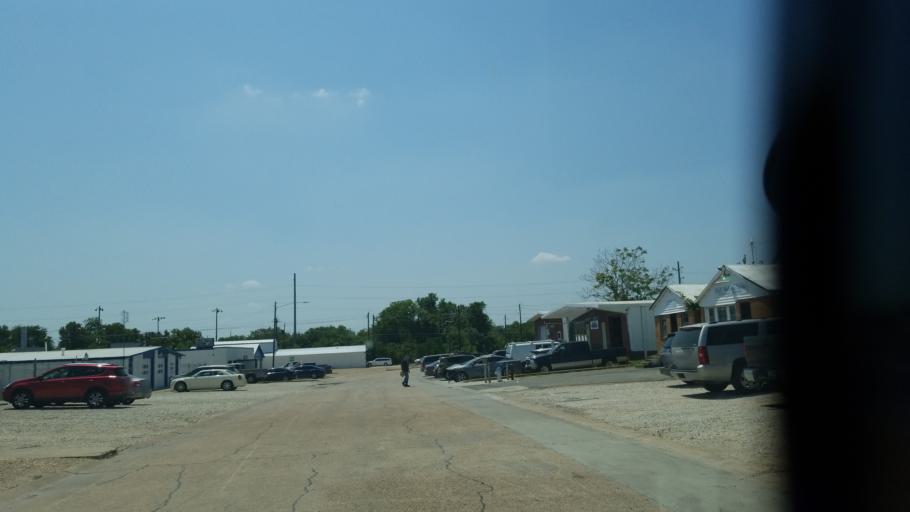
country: US
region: Texas
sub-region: Dallas County
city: Garland
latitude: 32.9124
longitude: -96.6267
